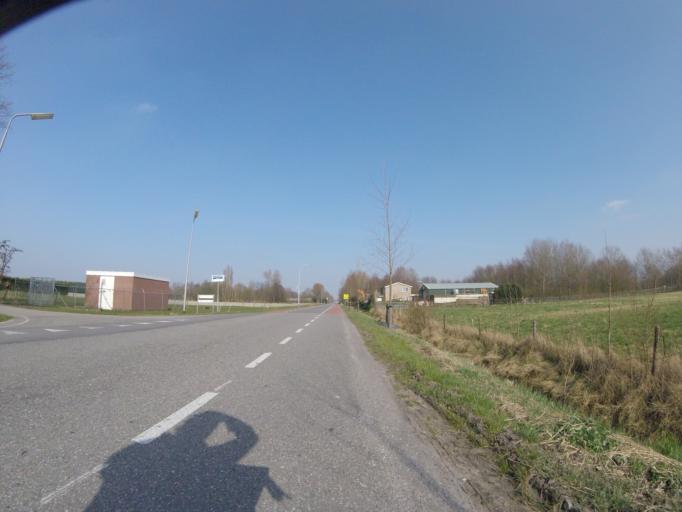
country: NL
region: North Holland
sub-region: Gemeente Heemstede
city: Heemstede
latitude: 52.3334
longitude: 4.6533
